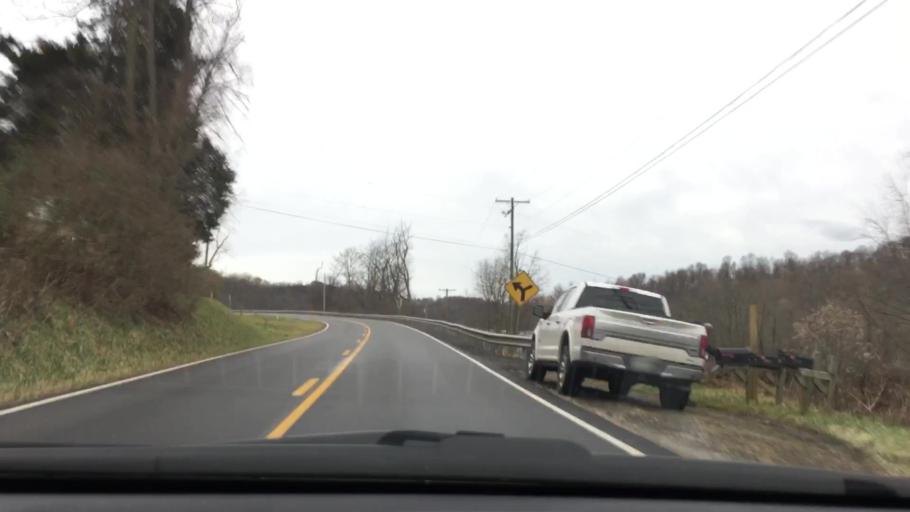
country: US
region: Pennsylvania
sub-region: Greene County
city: Morrisville
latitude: 39.8755
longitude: -80.1605
